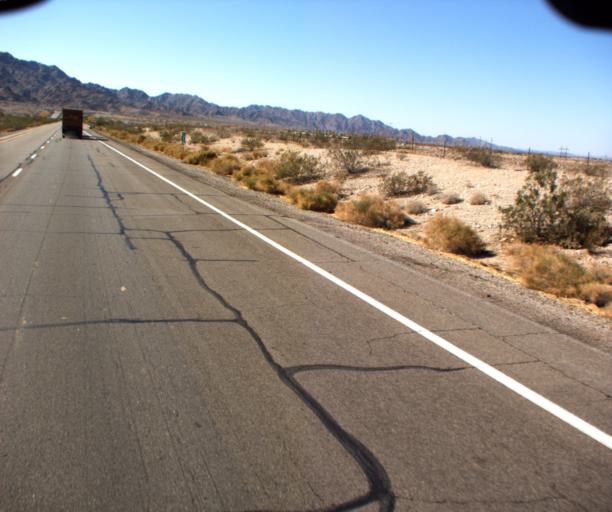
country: US
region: Arizona
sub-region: Yuma County
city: Fortuna Foothills
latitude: 32.6681
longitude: -114.2873
